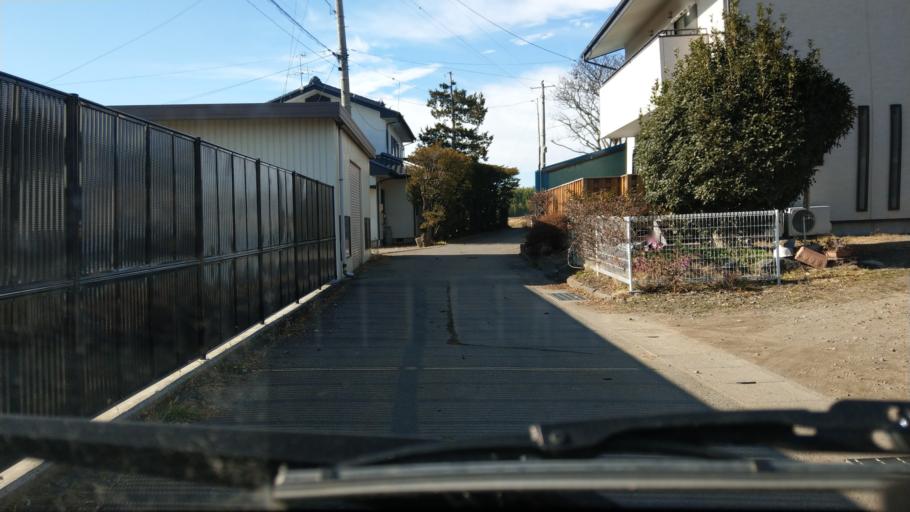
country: JP
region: Nagano
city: Komoro
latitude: 36.3250
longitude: 138.4550
